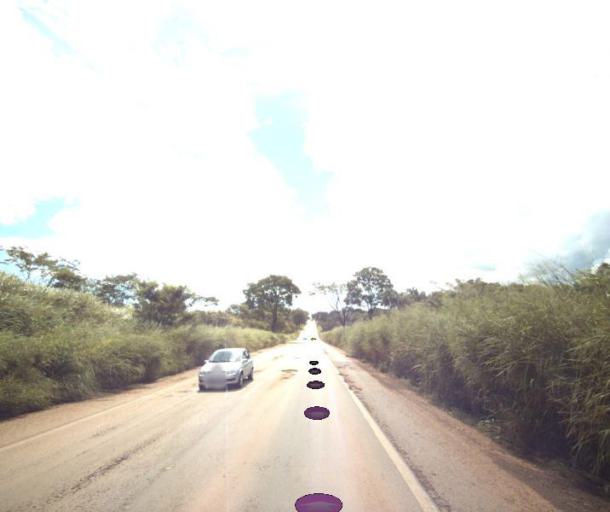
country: BR
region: Goias
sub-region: Petrolina De Goias
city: Petrolina de Goias
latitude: -15.9883
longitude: -49.1541
